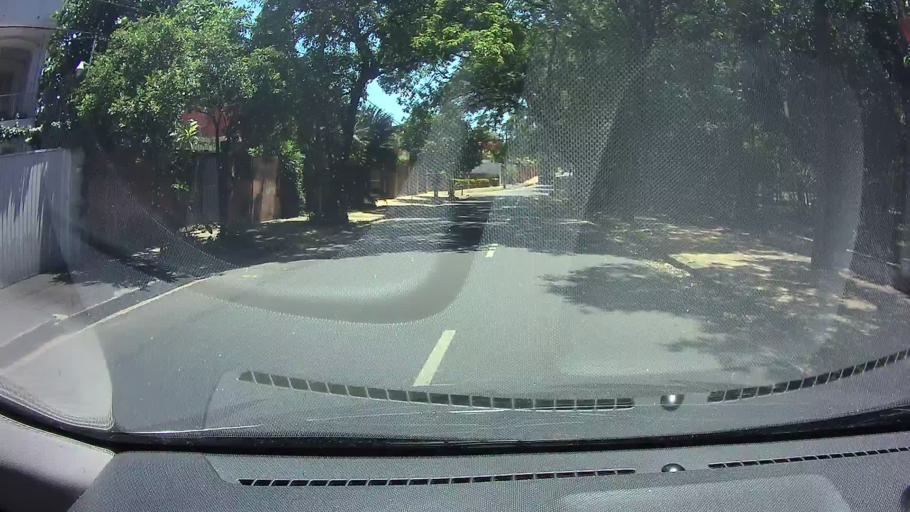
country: PY
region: Asuncion
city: Asuncion
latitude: -25.3021
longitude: -57.6039
